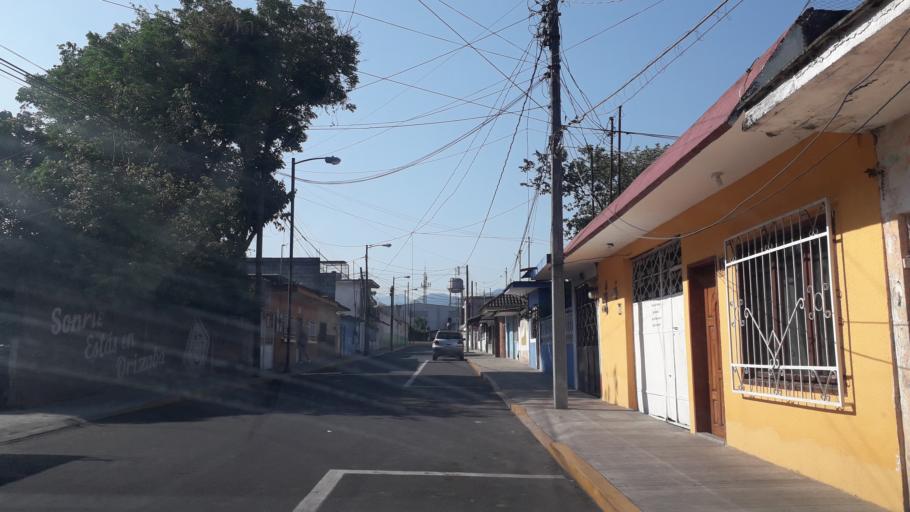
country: MX
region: Veracruz
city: Orizaba
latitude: 18.8440
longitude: -97.0912
